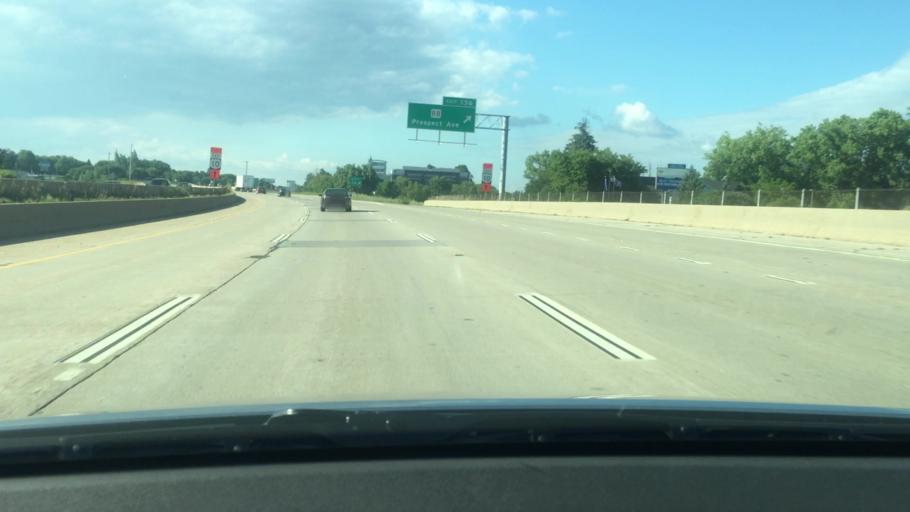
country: US
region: Wisconsin
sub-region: Winnebago County
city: Menasha
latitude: 44.2403
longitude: -88.4650
